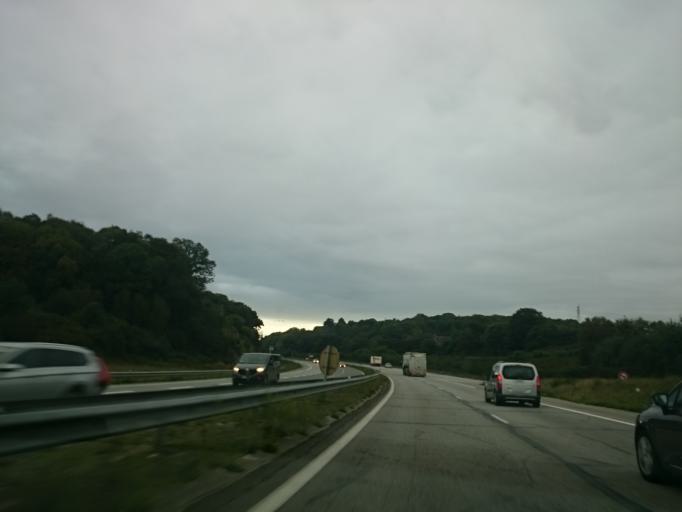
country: FR
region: Brittany
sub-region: Departement du Finistere
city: Quimper
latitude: 48.0285
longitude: -4.0863
